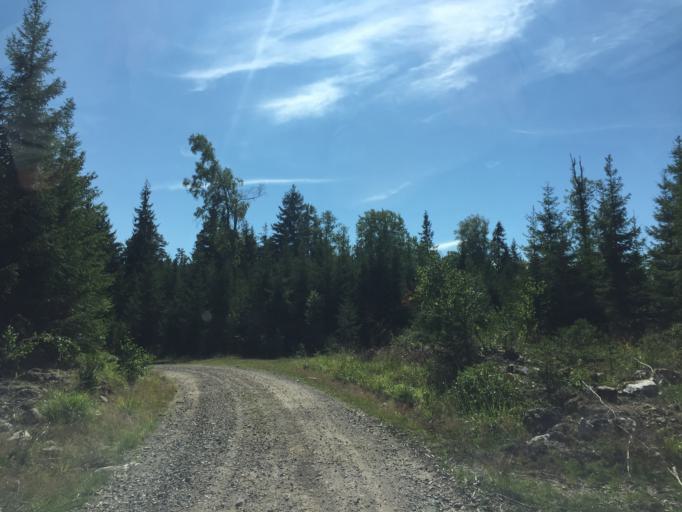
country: SE
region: OErebro
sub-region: Orebro Kommun
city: Odensbacken
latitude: 58.9312
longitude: 15.5807
